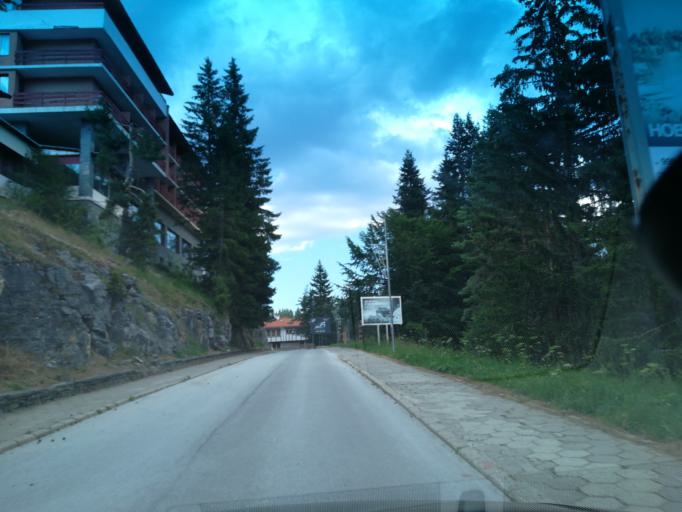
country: BG
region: Smolyan
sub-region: Obshtina Smolyan
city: Smolyan
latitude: 41.6557
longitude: 24.6948
